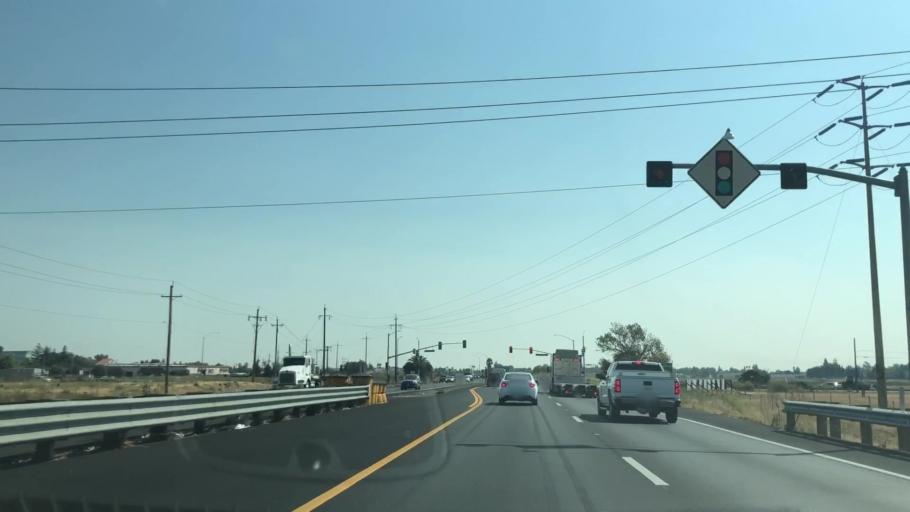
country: US
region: California
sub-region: Solano County
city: Suisun
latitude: 38.2410
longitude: -122.0524
